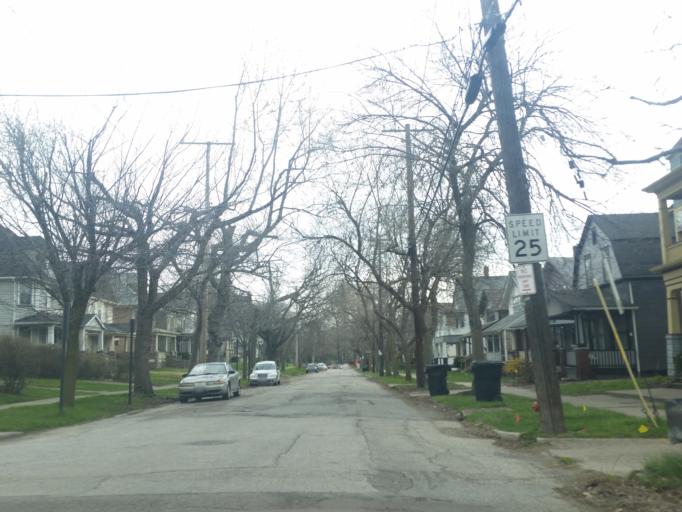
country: US
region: Ohio
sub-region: Cuyahoga County
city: Brooklyn Heights
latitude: 41.4544
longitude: -81.7039
